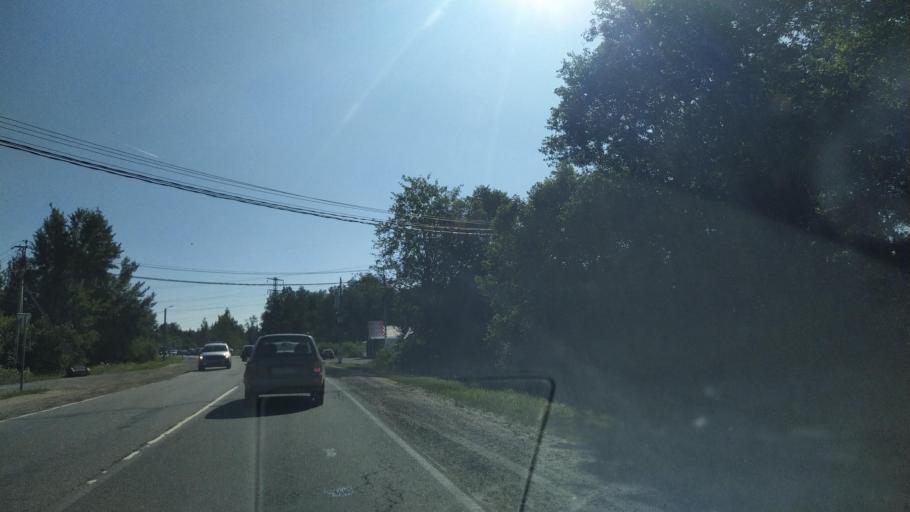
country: RU
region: Leningrad
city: Kirovsk
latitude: 59.9276
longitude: 30.9787
